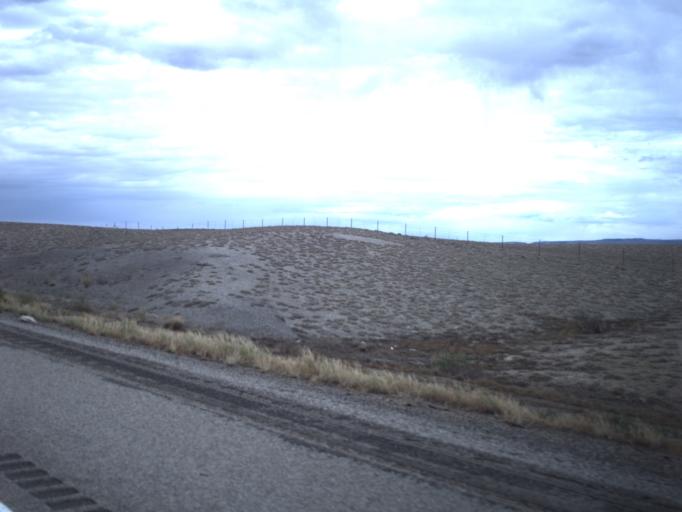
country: US
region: Utah
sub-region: Grand County
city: Moab
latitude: 38.9790
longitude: -109.3462
